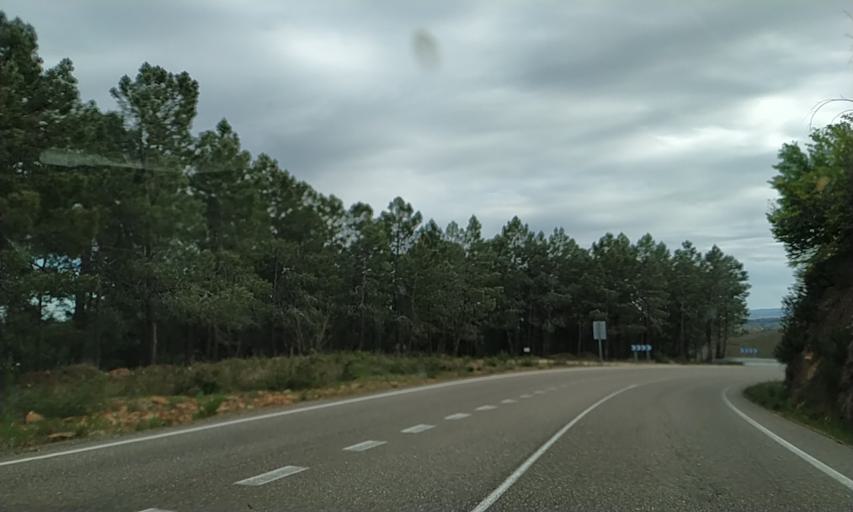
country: ES
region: Extremadura
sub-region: Provincia de Caceres
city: Acebo
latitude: 40.2009
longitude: -6.6713
